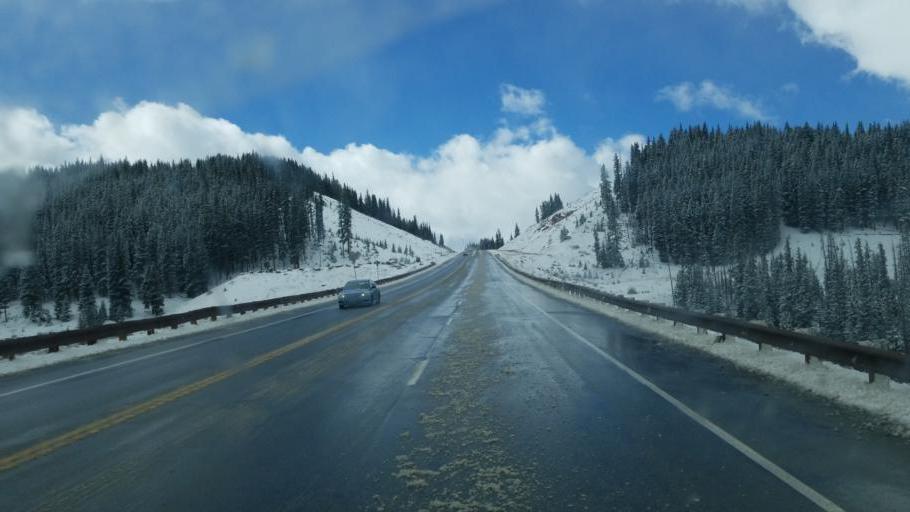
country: US
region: Colorado
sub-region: Summit County
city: Breckenridge
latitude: 39.4147
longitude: -106.1740
